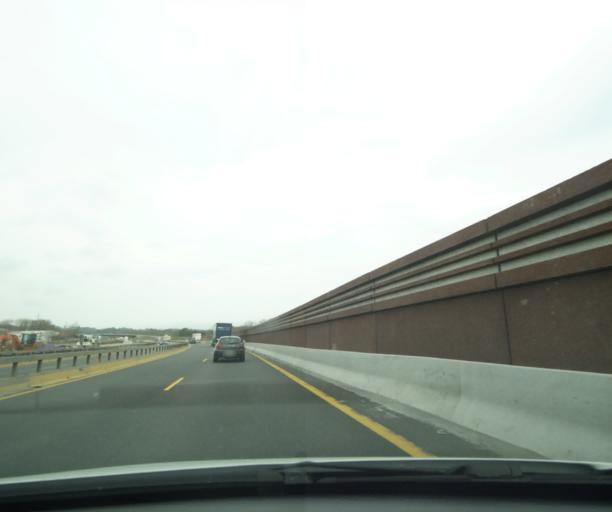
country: FR
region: Aquitaine
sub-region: Departement des Pyrenees-Atlantiques
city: Bidart
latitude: 43.4326
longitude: -1.5760
